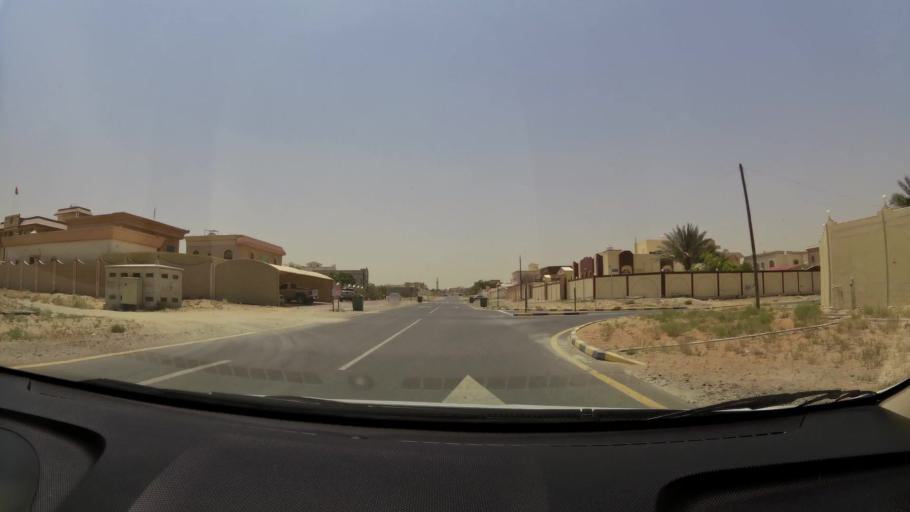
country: AE
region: Ajman
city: Ajman
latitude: 25.4085
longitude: 55.5191
